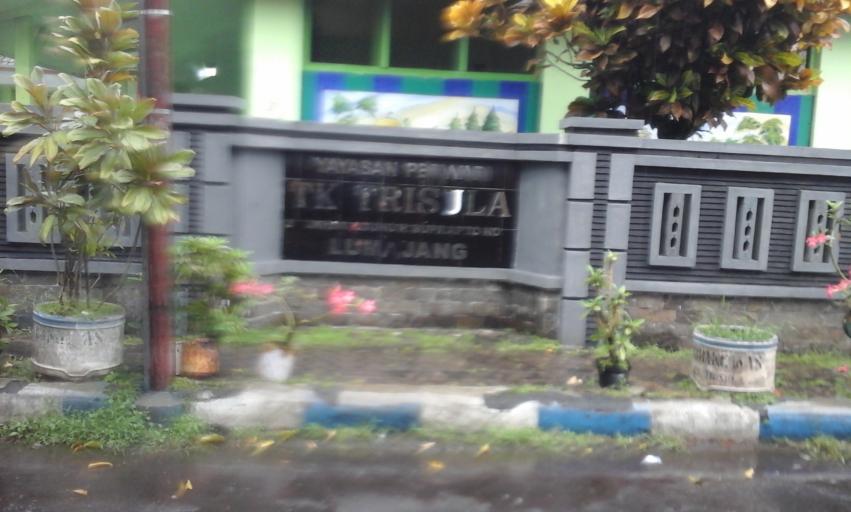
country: ID
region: East Java
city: Lumajang
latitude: -8.1355
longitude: 113.2275
